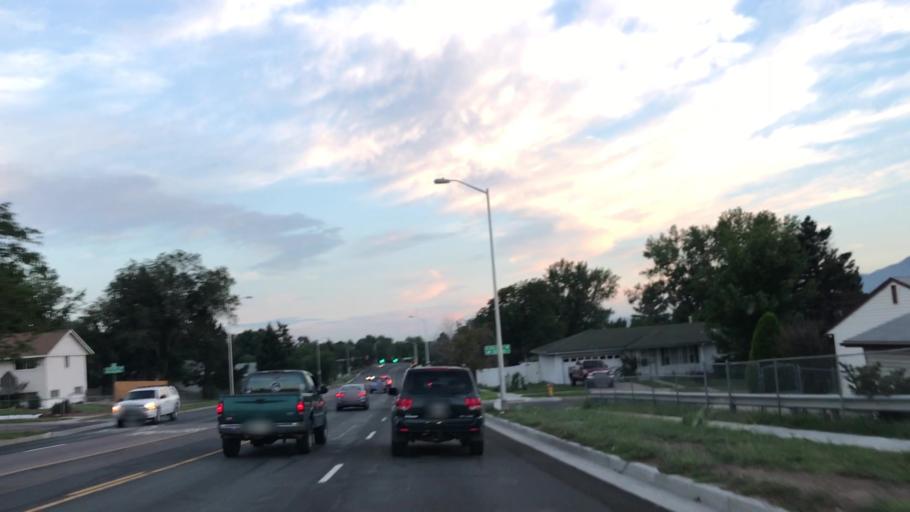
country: US
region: Colorado
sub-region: El Paso County
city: Colorado Springs
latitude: 38.8319
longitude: -104.7760
